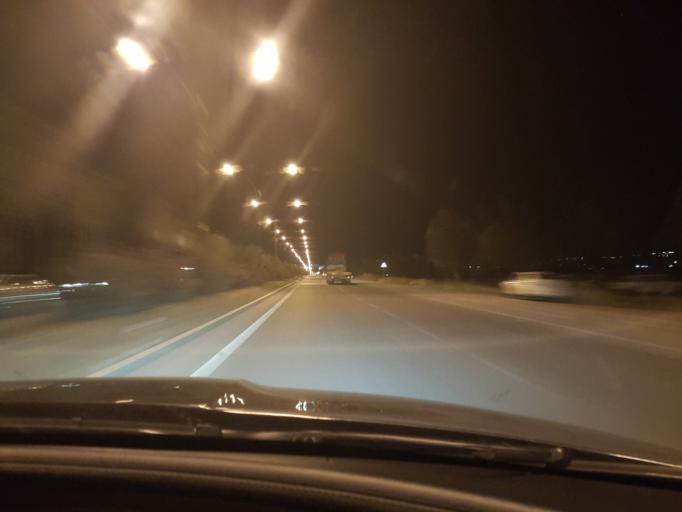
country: IQ
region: Arbil
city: Erbil
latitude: 36.2694
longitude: 44.0956
